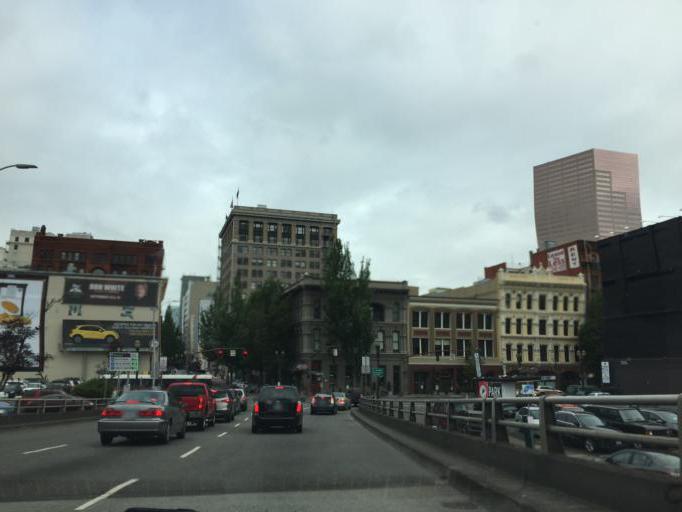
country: US
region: Oregon
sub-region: Multnomah County
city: Portland
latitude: 45.5190
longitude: -122.6731
